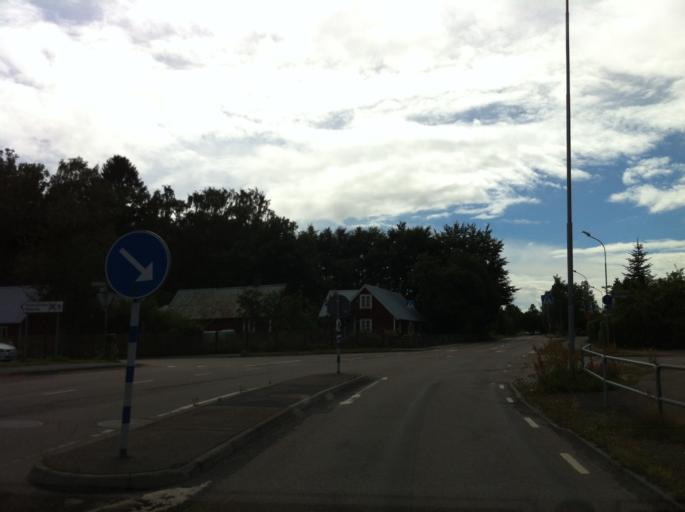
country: SE
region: Skane
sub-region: Hassleholms Kommun
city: Tormestorp
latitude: 56.1869
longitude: 13.6754
